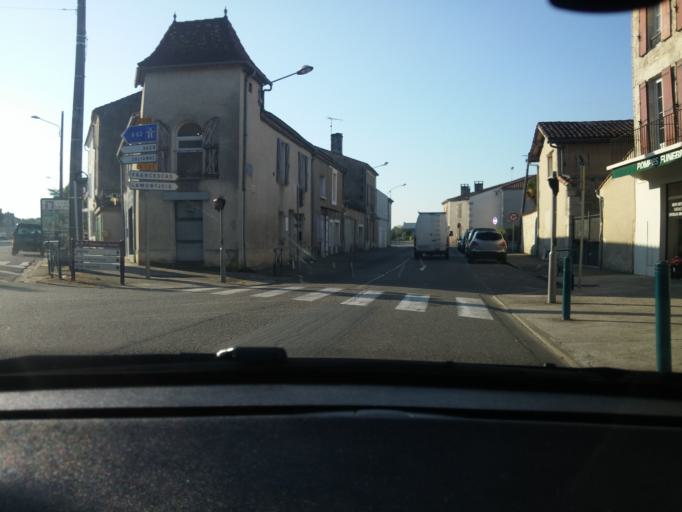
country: FR
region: Aquitaine
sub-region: Departement du Lot-et-Garonne
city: Nerac
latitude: 44.1341
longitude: 0.3450
